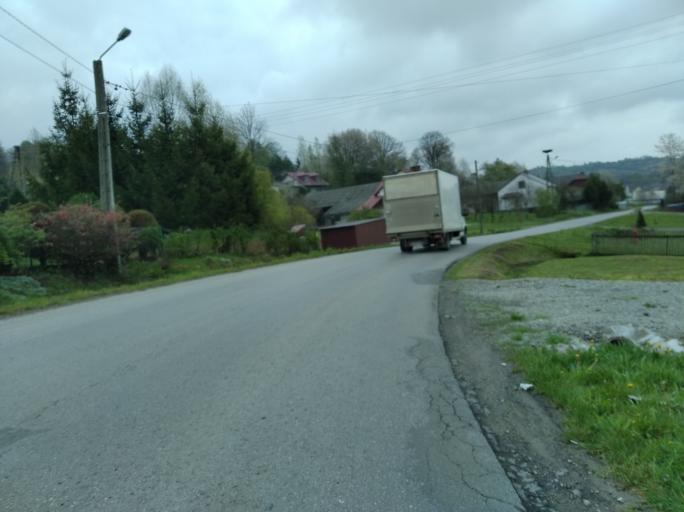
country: PL
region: Subcarpathian Voivodeship
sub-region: Powiat brzozowski
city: Domaradz
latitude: 49.7921
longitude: 21.9707
